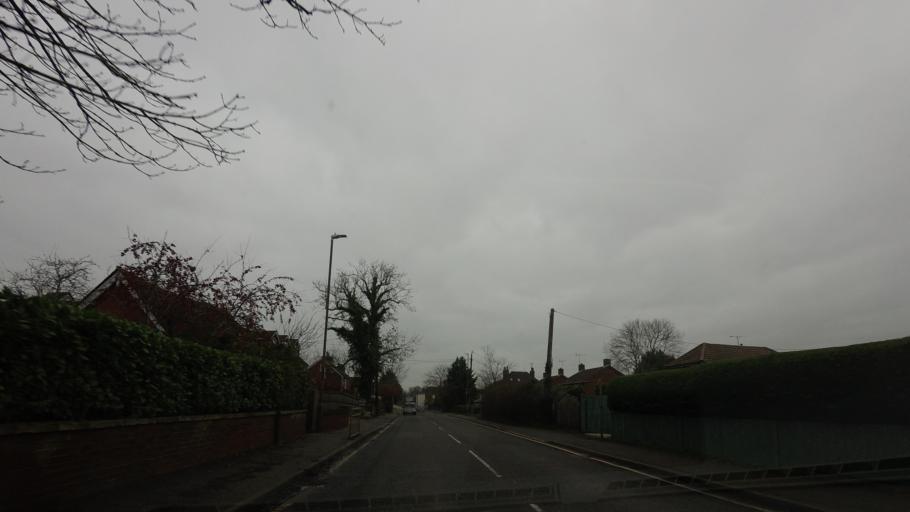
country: GB
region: England
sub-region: Kent
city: Staplehurst
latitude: 51.1683
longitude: 0.5526
